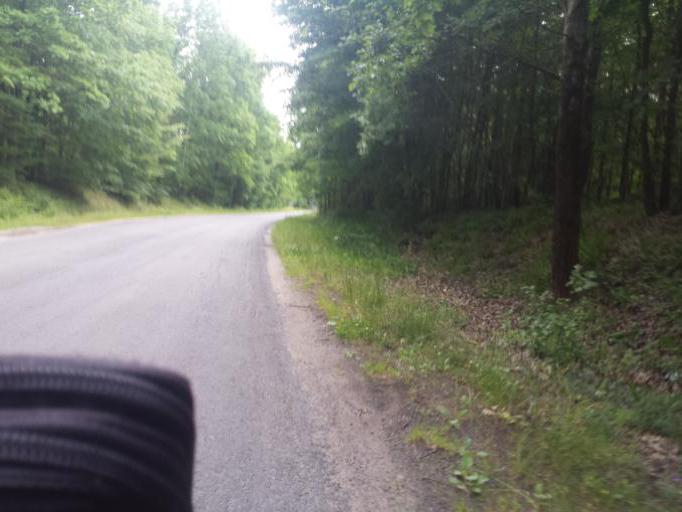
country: PL
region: Warmian-Masurian Voivodeship
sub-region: Powiat ilawski
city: Ilawa
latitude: 53.5671
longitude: 19.5672
